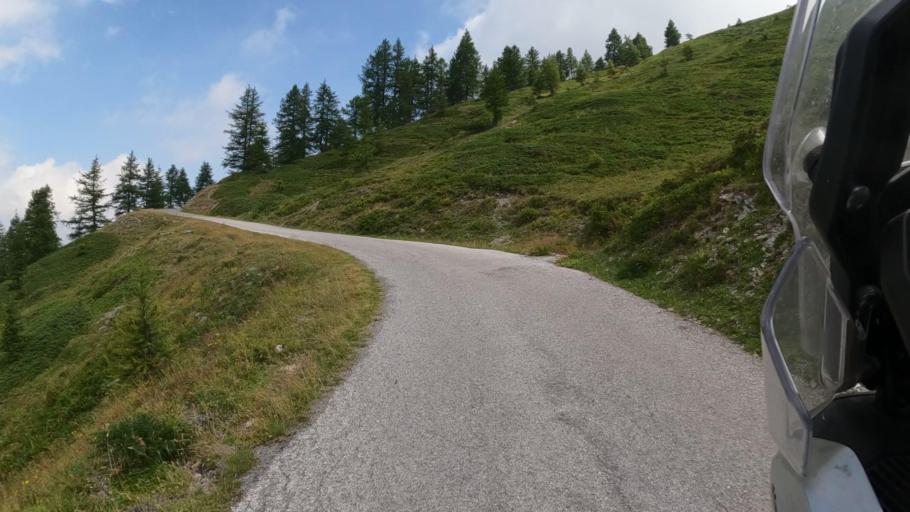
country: IT
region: Piedmont
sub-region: Provincia di Cuneo
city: Marmora
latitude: 44.4038
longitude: 7.1139
